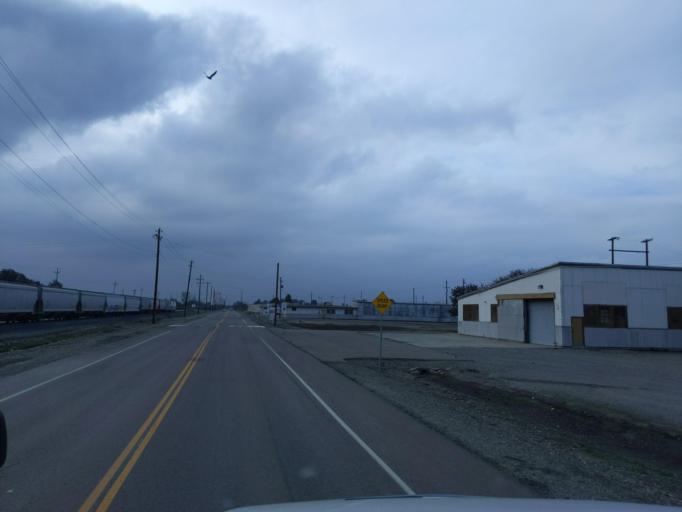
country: US
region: California
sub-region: San Joaquin County
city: Country Club
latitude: 37.9490
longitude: -121.3622
